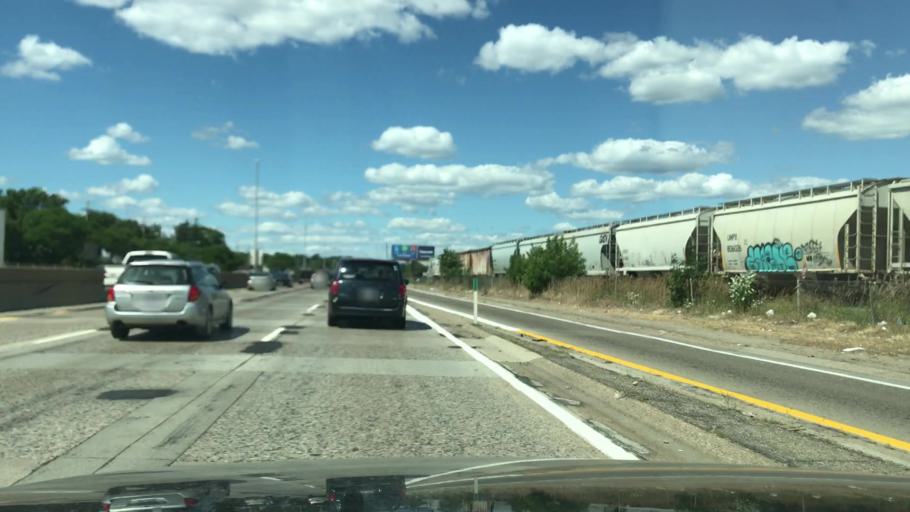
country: US
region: Michigan
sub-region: Kent County
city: Wyoming
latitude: 42.9298
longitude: -85.6813
